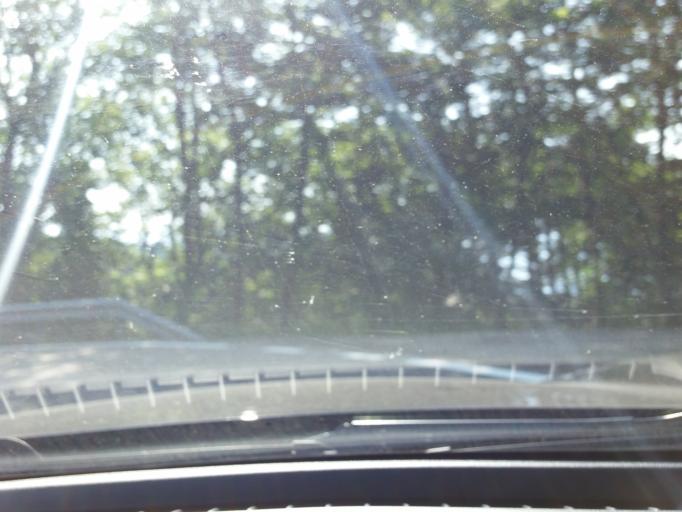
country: IT
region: Trentino-Alto Adige
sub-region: Bolzano
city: Caldaro sulla Strada del Vino
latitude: 46.4345
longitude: 11.2323
